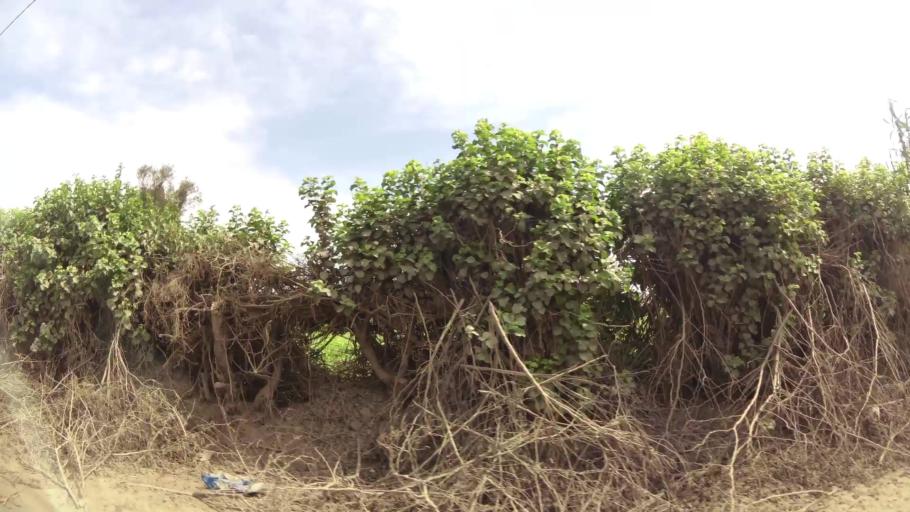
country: PE
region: Lima
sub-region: Provincia de Canete
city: Mala
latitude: -12.7315
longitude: -76.6220
